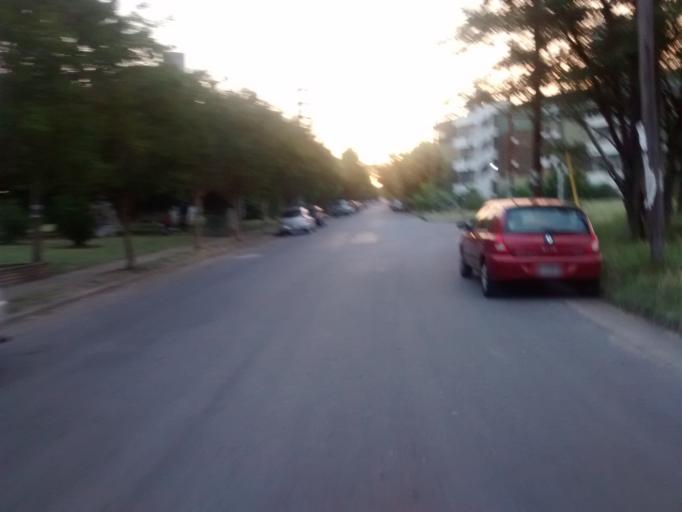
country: AR
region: Buenos Aires
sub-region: Partido de La Plata
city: La Plata
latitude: -34.9422
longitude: -57.9210
